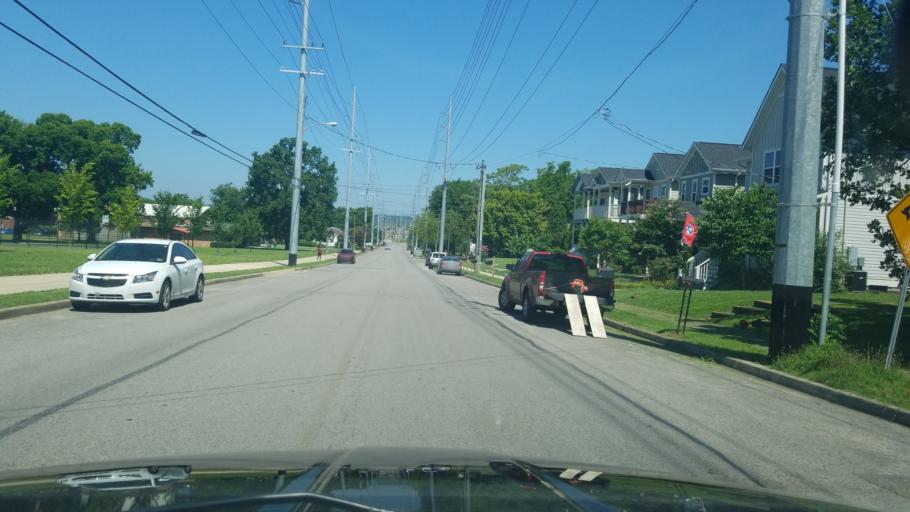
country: US
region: Tennessee
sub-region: Davidson County
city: Belle Meade
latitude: 36.1627
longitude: -86.8618
